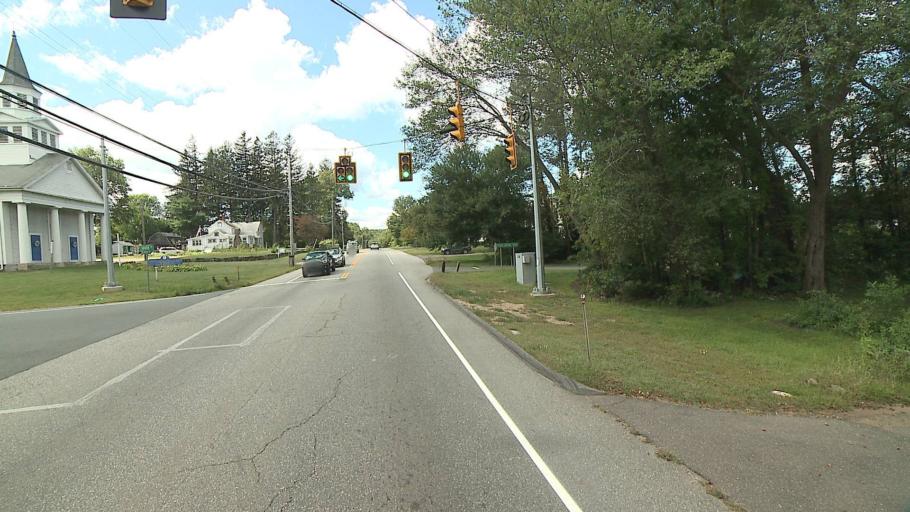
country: US
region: Connecticut
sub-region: Tolland County
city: Rockville
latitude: 41.7965
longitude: -72.4281
